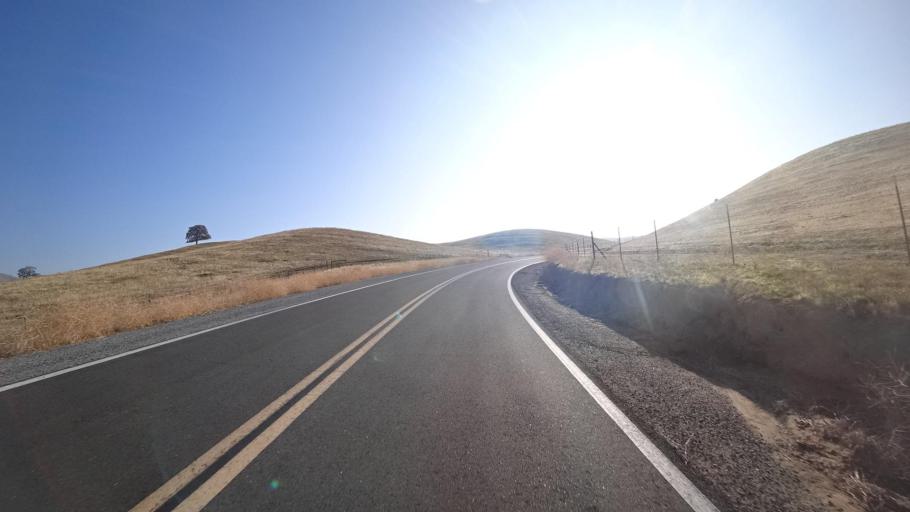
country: US
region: California
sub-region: Tulare County
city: Richgrove
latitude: 35.7439
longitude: -118.8795
